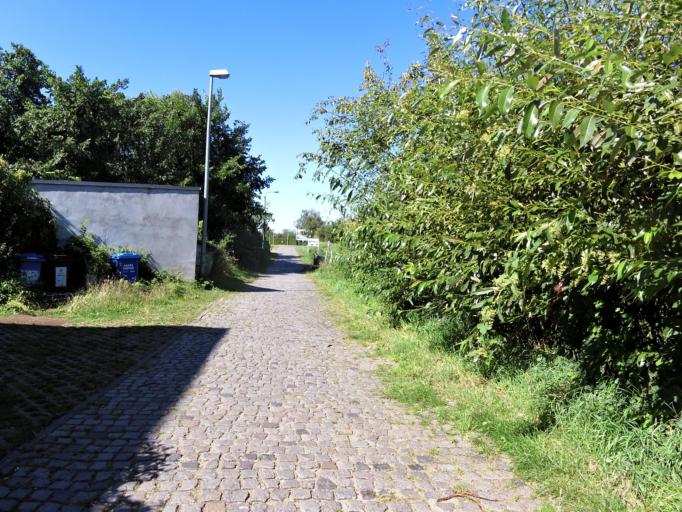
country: DE
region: Saxony-Anhalt
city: Wittenburg
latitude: 51.8631
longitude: 12.6793
